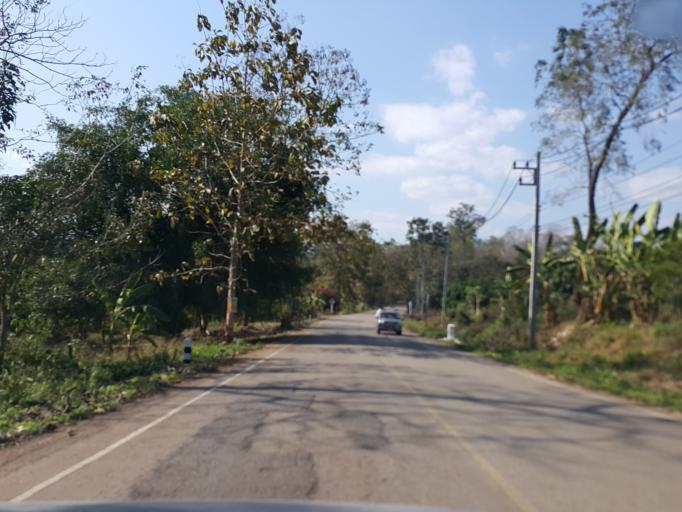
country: TH
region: Chiang Mai
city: Mae Wang
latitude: 18.6476
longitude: 98.6947
